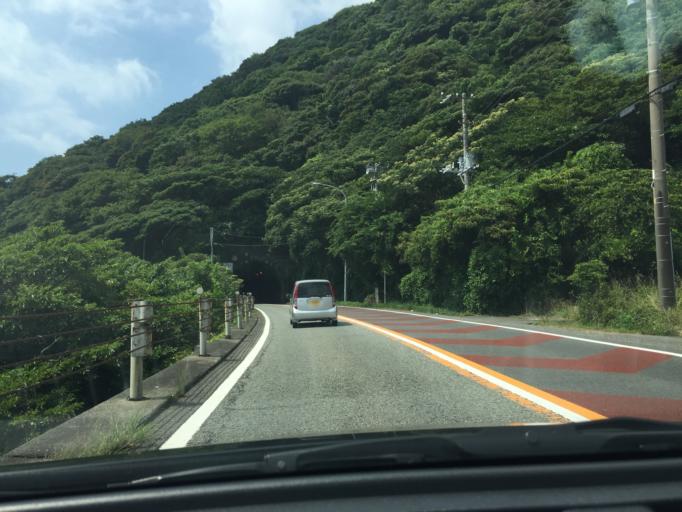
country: JP
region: Shizuoka
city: Shimoda
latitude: 34.7896
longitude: 139.0594
